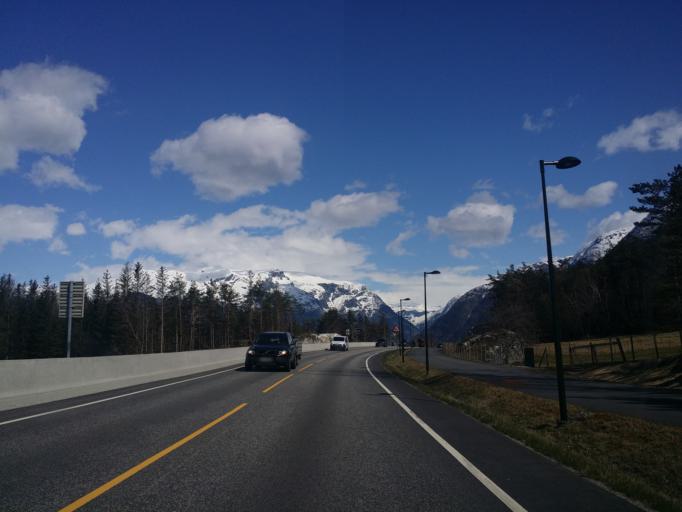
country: NO
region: Hordaland
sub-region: Ulvik
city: Ulvik
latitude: 60.4700
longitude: 6.8581
